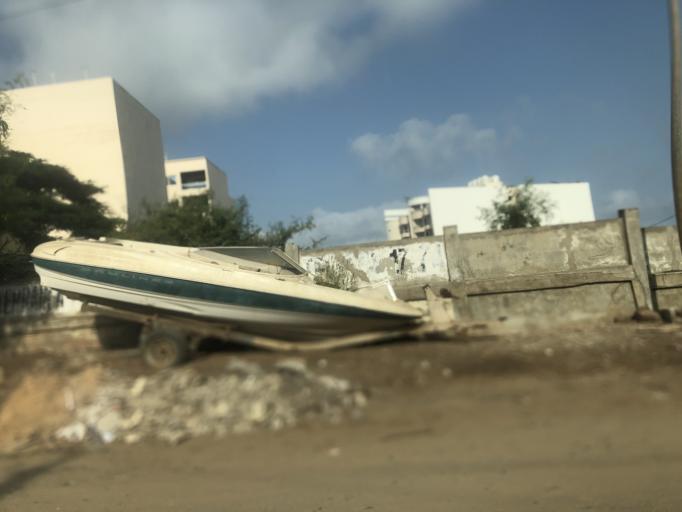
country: SN
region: Dakar
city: Mermoz Boabab
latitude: 14.7417
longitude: -17.5144
